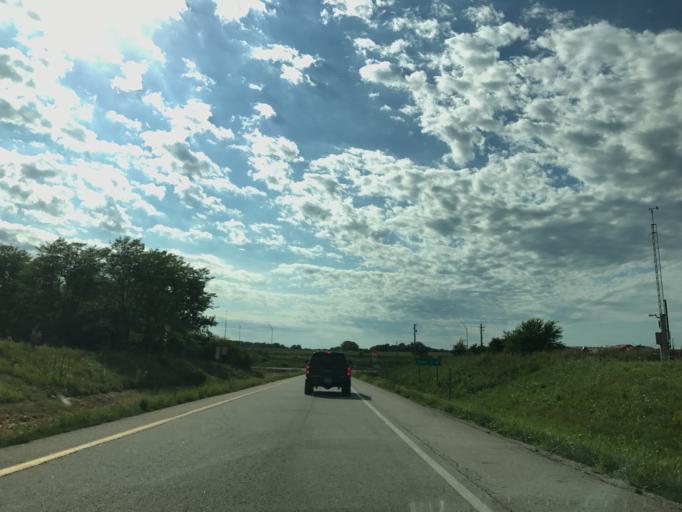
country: US
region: Iowa
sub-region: Dallas County
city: De Soto
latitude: 41.5413
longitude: -94.0105
